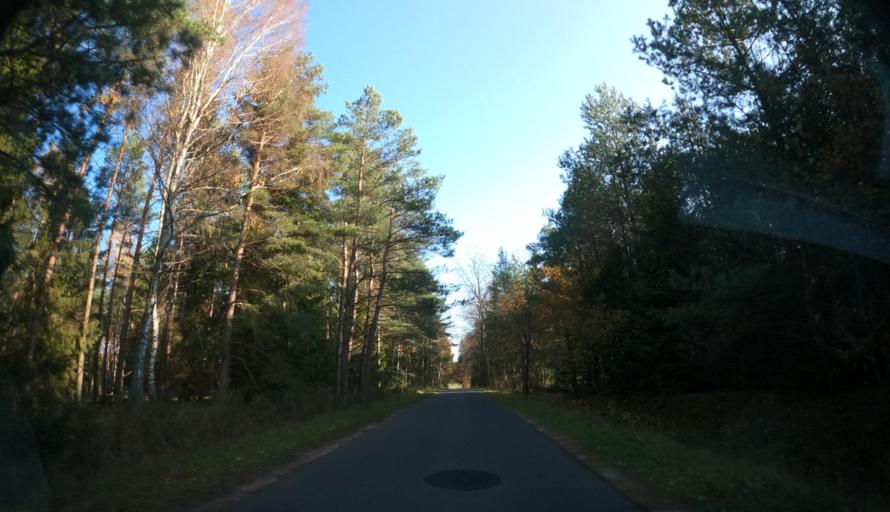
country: PL
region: Pomeranian Voivodeship
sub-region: Powiat slupski
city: Kepice
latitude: 54.2325
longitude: 16.7595
